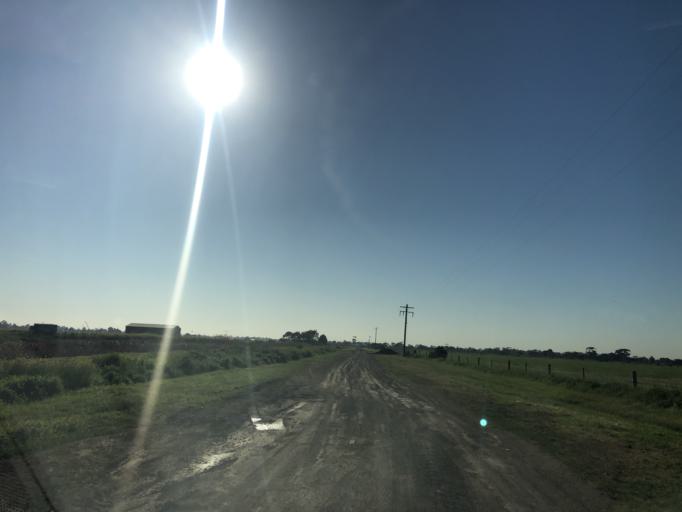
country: AU
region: Victoria
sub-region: Wyndham
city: Hoppers Crossing
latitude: -37.9137
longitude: 144.7008
